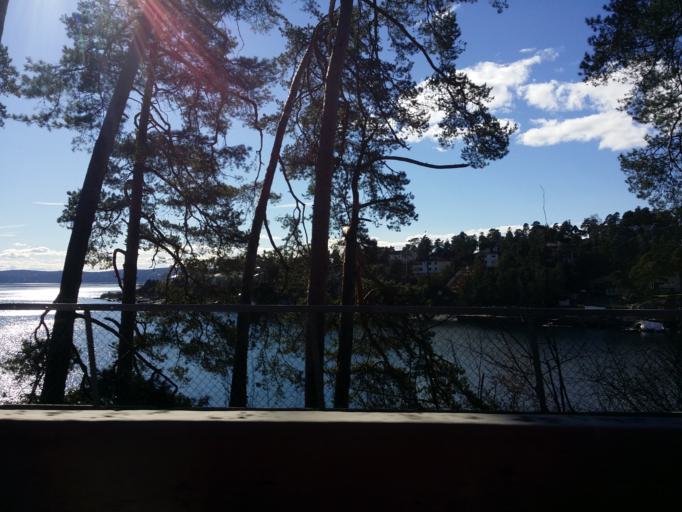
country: NO
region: Oslo
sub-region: Oslo
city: Oslo
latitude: 59.8706
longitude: 10.7811
